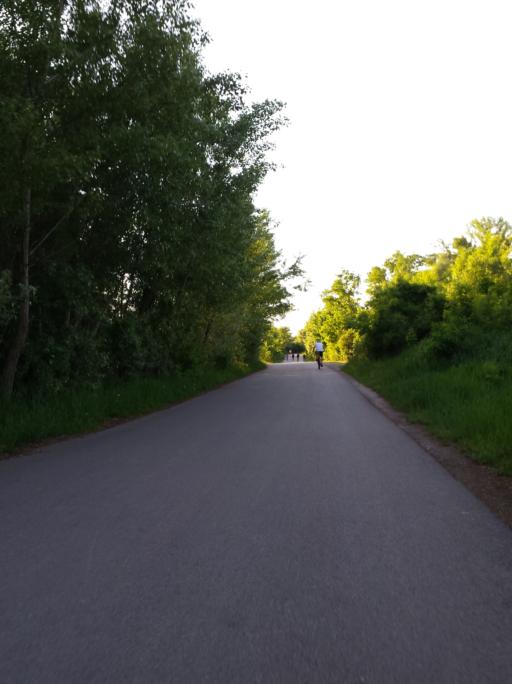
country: AT
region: Vienna
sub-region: Wien Stadt
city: Vienna
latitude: 48.2164
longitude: 16.4250
